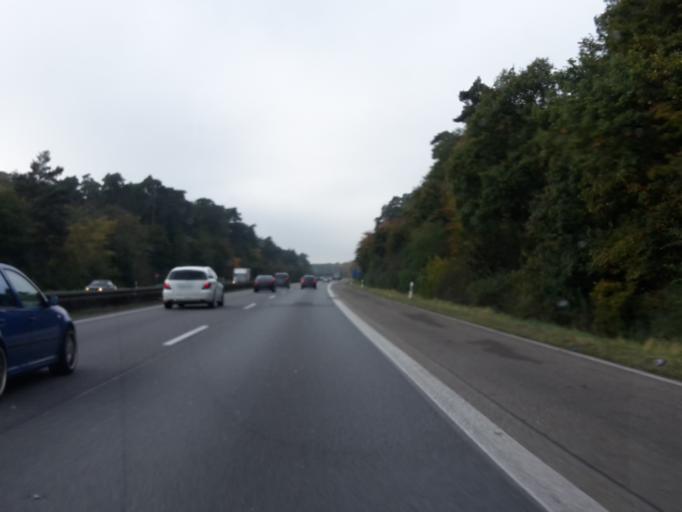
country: DE
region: Hesse
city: Raunheim
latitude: 50.0074
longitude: 8.4885
